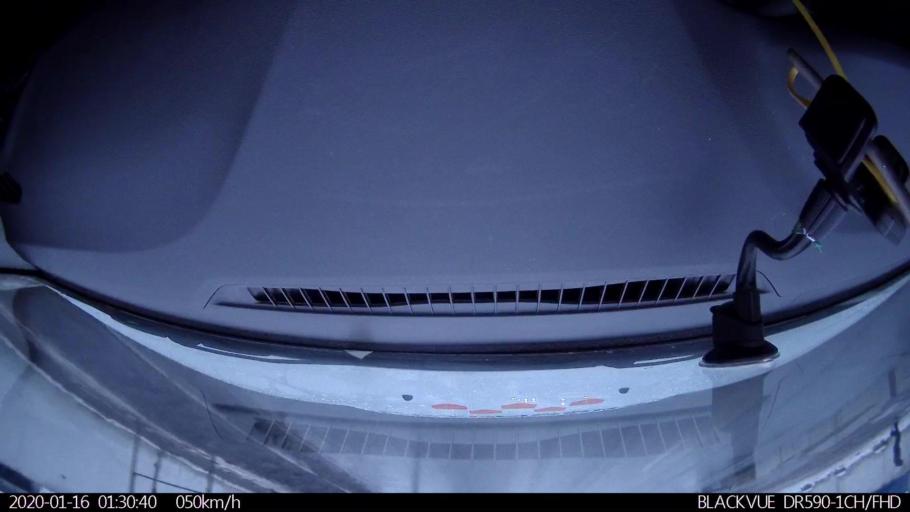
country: RU
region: Nizjnij Novgorod
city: Gorbatovka
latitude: 56.3412
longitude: 43.8160
